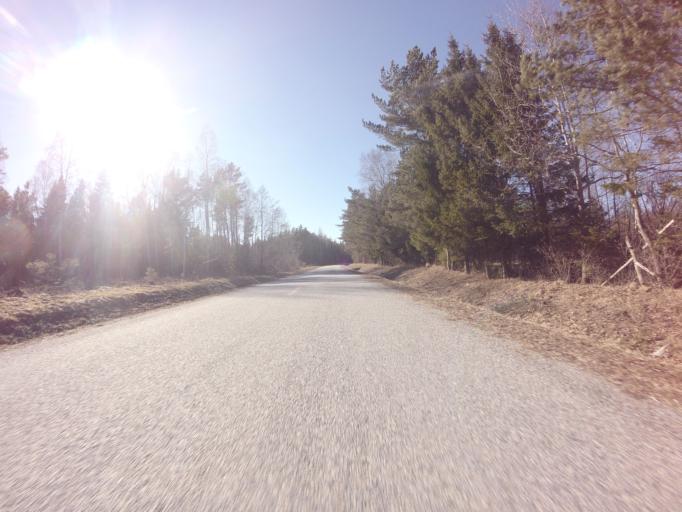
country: EE
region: Saare
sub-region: Kuressaare linn
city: Kuressaare
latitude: 58.5692
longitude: 22.4176
